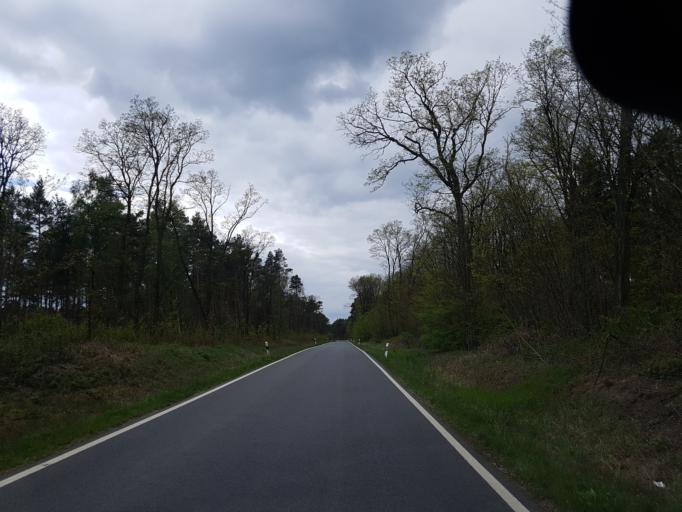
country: DE
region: Brandenburg
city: Altdobern
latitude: 51.6480
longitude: 13.9830
